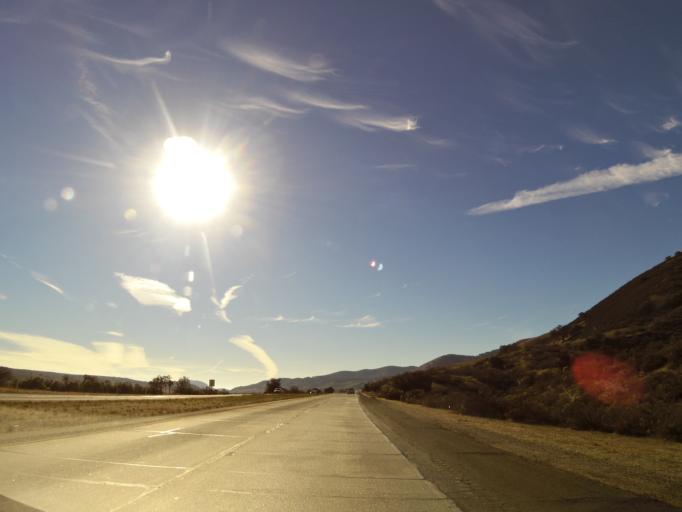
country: US
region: California
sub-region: San Luis Obispo County
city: Lake Nacimiento
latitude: 35.9465
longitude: -120.8759
